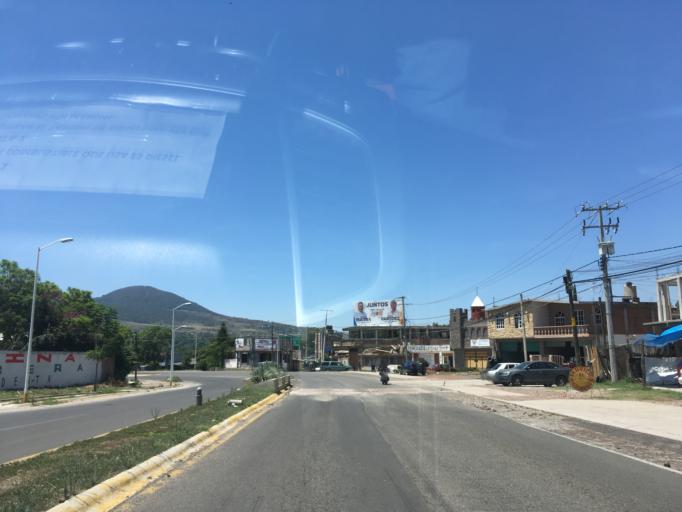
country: MX
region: Michoacan
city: Tuxpan
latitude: 19.5723
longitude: -100.4670
